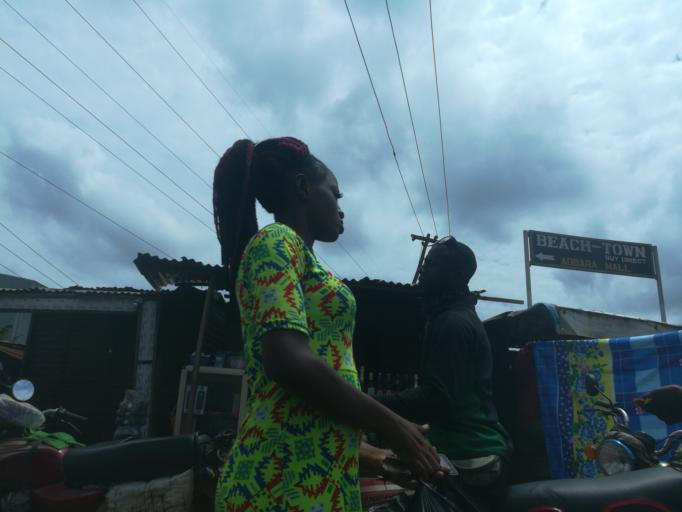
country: NG
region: Lagos
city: Ikotun
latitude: 6.4981
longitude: 3.0887
